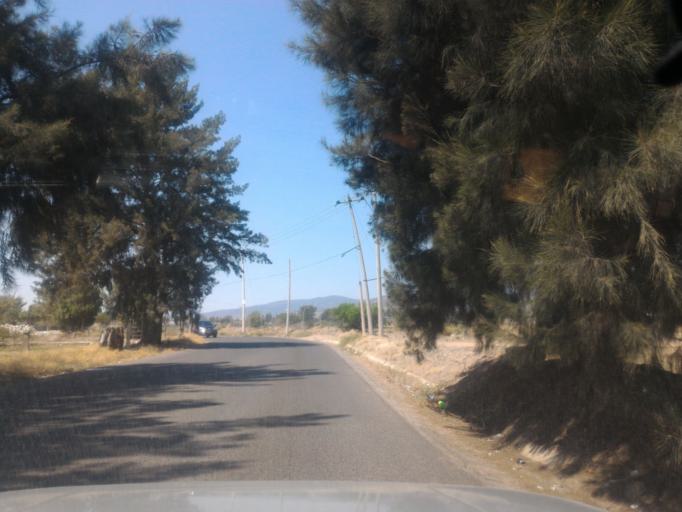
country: MX
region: Jalisco
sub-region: San Pedro Tlaquepaque
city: Santa Anita
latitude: 20.5591
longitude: -103.4191
